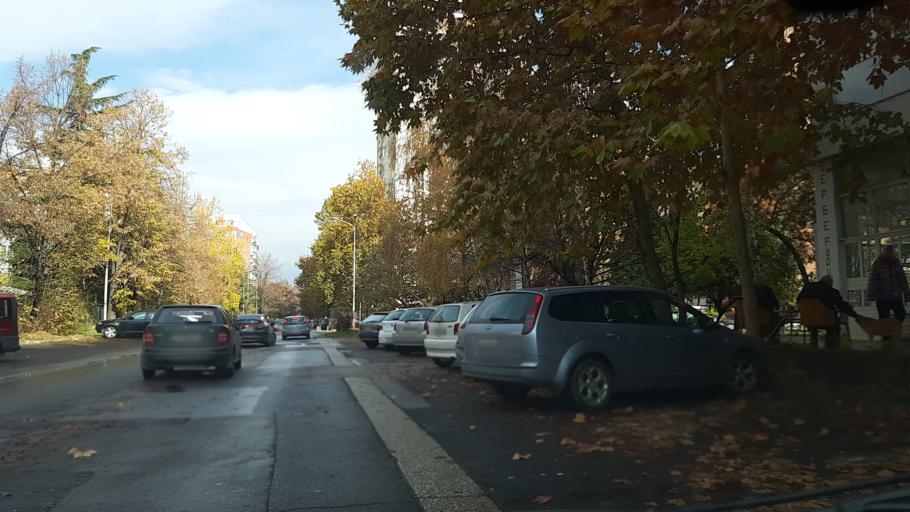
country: MK
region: Kisela Voda
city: Usje
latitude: 41.9868
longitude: 21.4668
